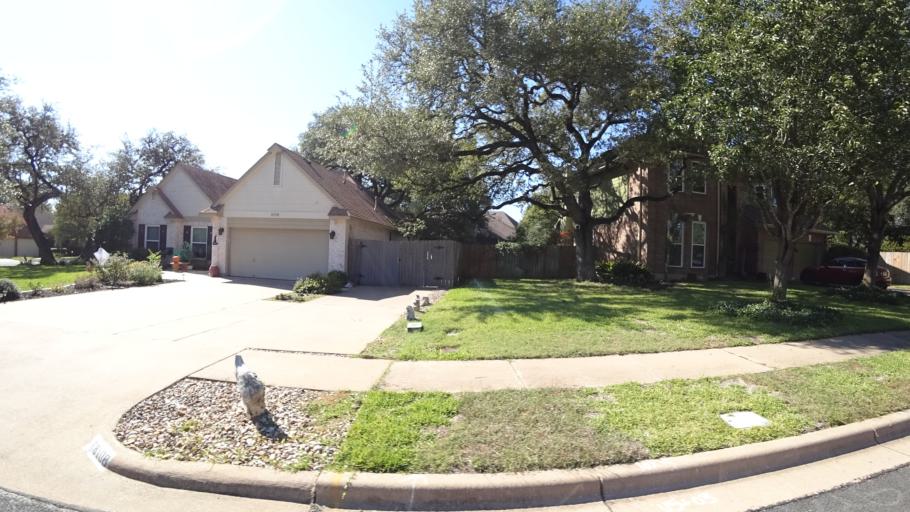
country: US
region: Texas
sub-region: Travis County
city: Shady Hollow
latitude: 30.2174
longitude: -97.8725
